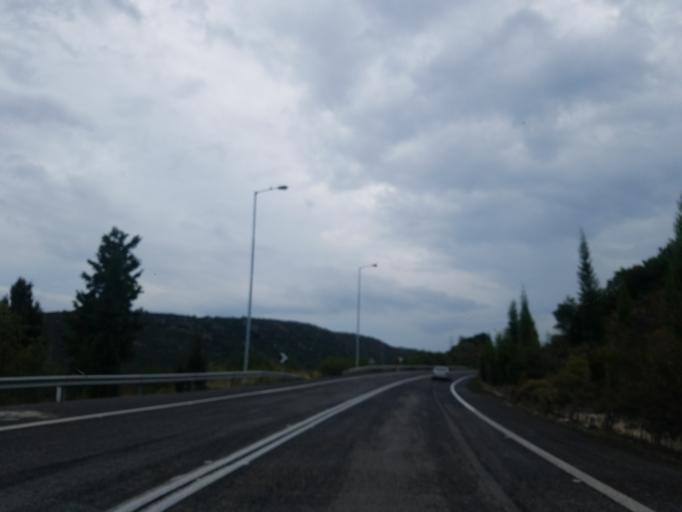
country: GR
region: Central Greece
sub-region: Nomos Voiotias
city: Livadeia
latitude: 38.4472
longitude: 22.7947
